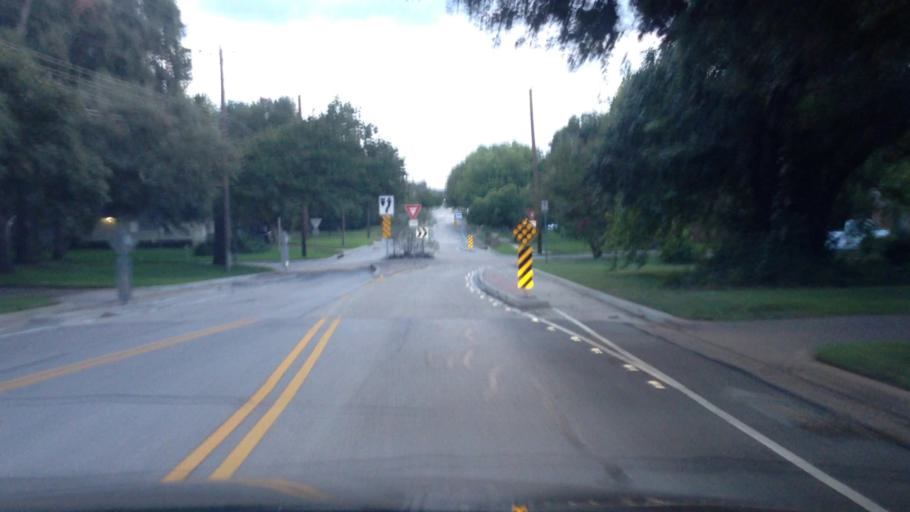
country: US
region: Texas
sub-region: Tarrant County
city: Pantego
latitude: 32.7318
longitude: -97.1358
